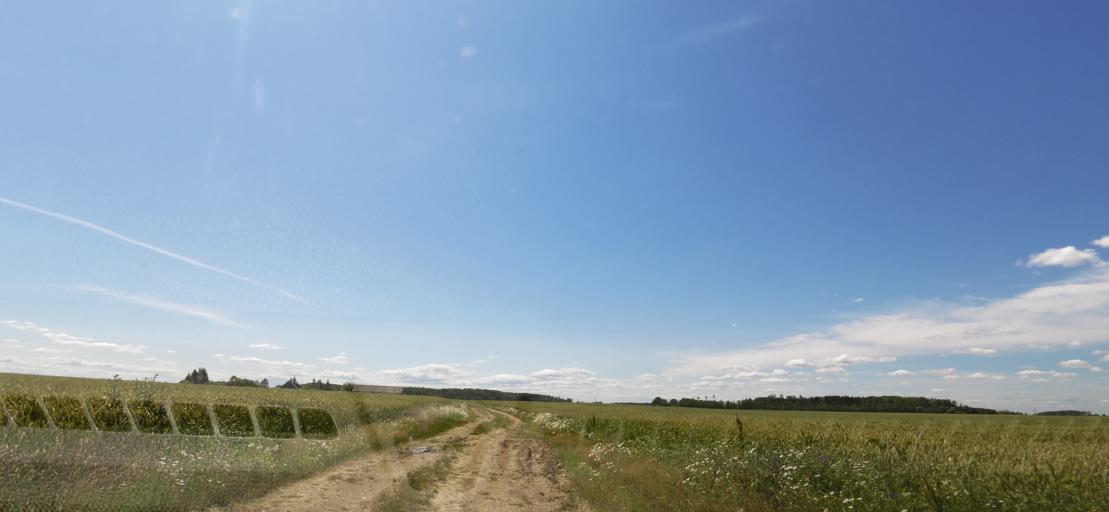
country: LT
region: Panevezys
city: Pasvalys
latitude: 56.2691
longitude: 24.5135
